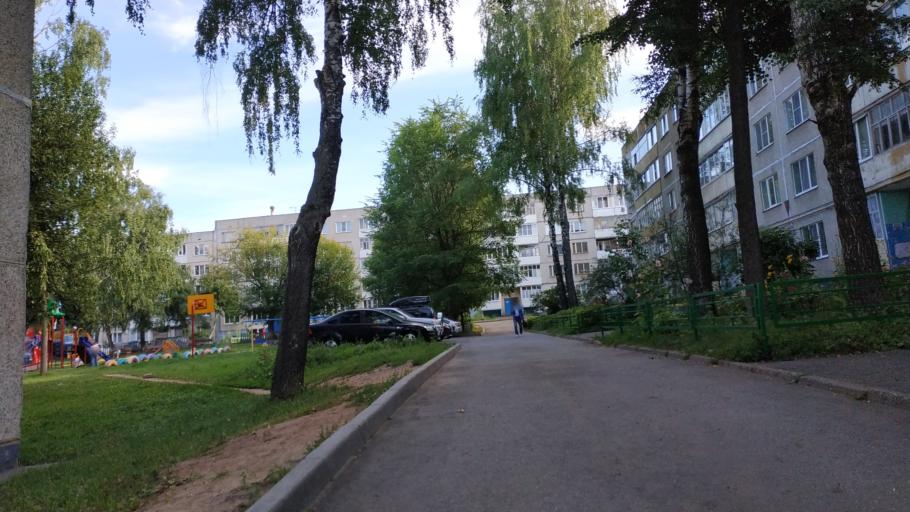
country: RU
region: Chuvashia
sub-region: Cheboksarskiy Rayon
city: Cheboksary
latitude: 56.1440
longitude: 47.1827
